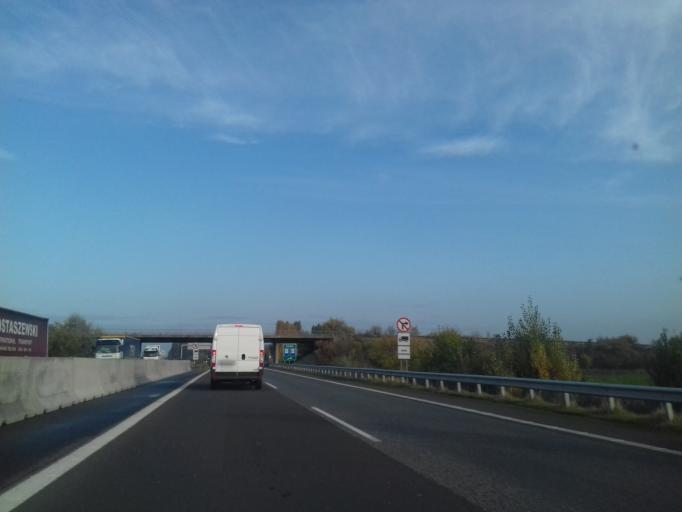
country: SK
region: Bratislavsky
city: Stupava
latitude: 48.2554
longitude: 17.0111
